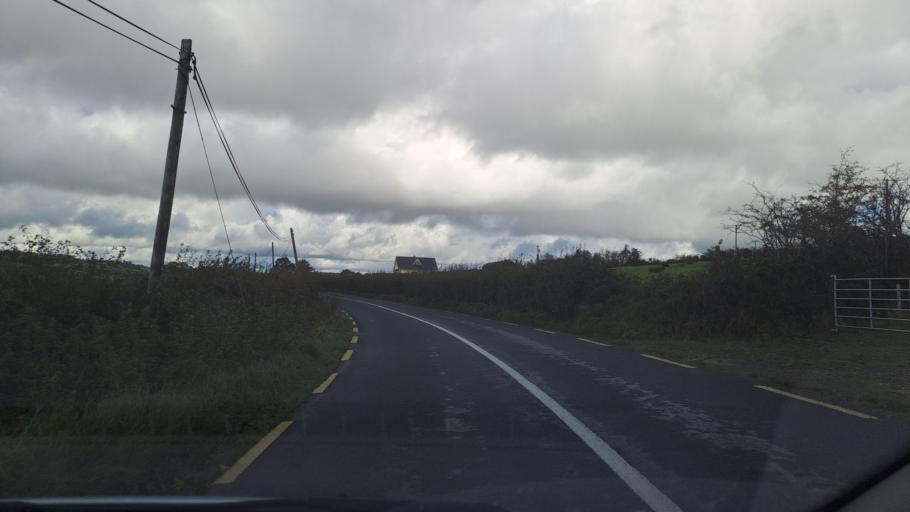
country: IE
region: Ulster
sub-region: An Cabhan
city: Bailieborough
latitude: 53.8742
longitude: -6.9650
